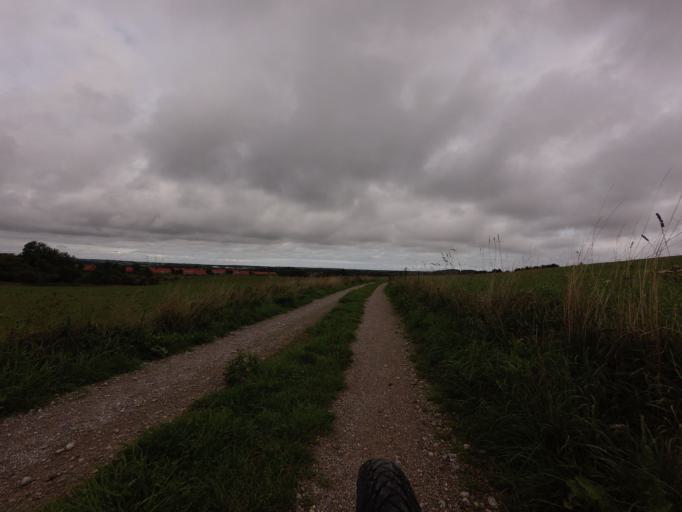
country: DK
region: North Denmark
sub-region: Hjorring Kommune
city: Hjorring
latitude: 57.4701
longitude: 9.9795
